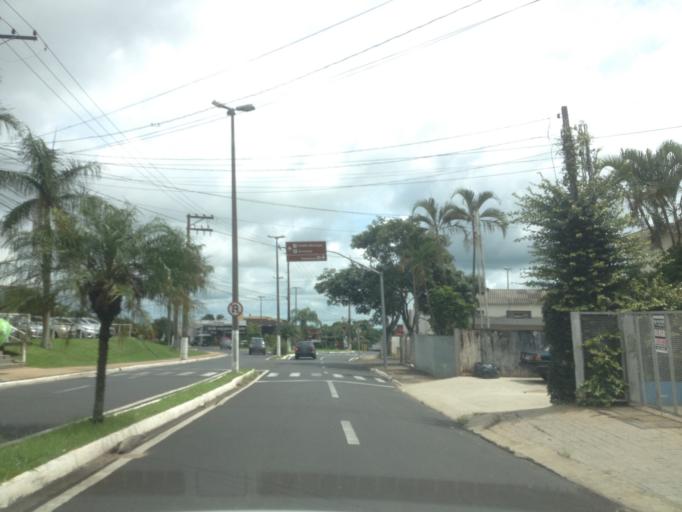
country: BR
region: Sao Paulo
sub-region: Marilia
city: Marilia
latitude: -22.2275
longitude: -49.9305
